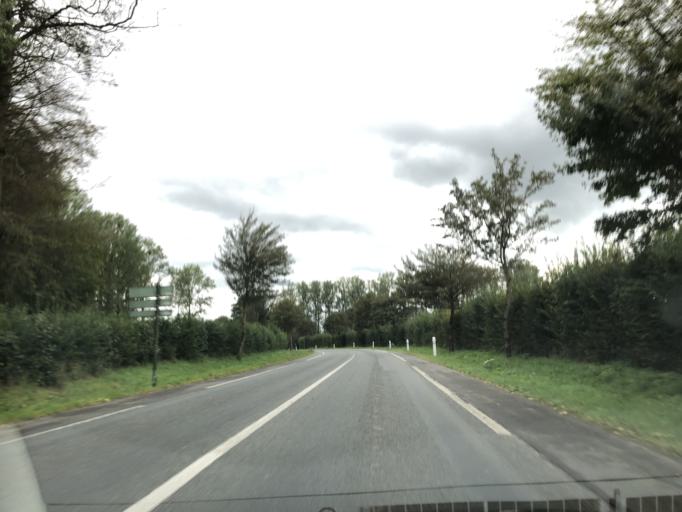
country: FR
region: Nord-Pas-de-Calais
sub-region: Departement du Pas-de-Calais
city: Fruges
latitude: 50.4825
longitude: 2.1229
